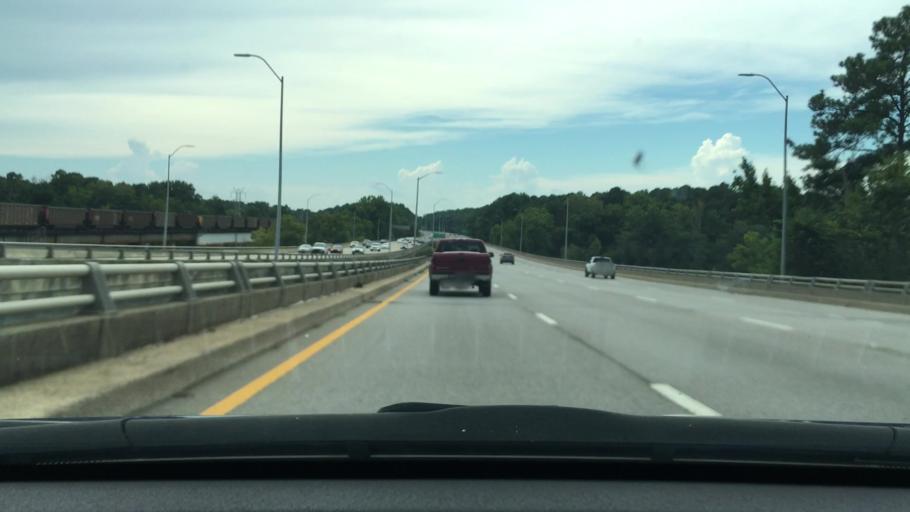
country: US
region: South Carolina
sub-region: Lexington County
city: West Columbia
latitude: 34.0091
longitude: -81.0585
